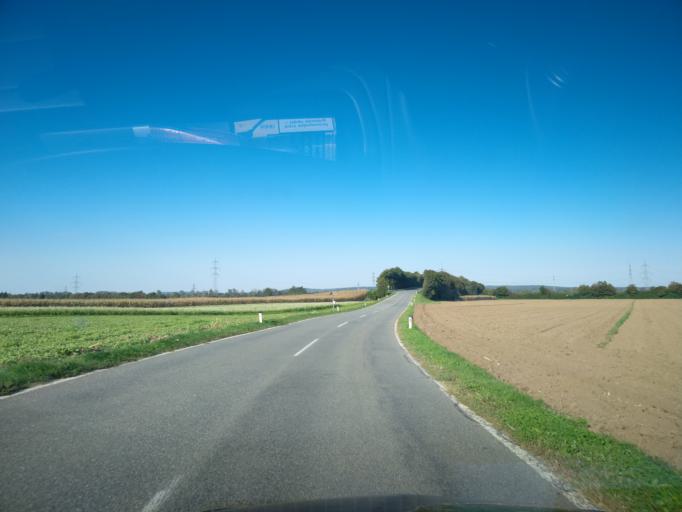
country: AT
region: Styria
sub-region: Politischer Bezirk Leibnitz
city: Kaindorf an der Sulm
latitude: 46.8184
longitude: 15.5569
